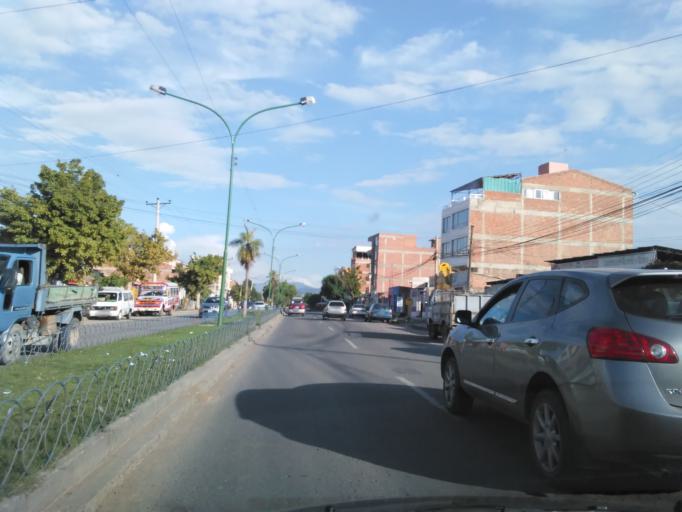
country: BO
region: Cochabamba
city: Cochabamba
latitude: -17.3554
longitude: -66.1866
